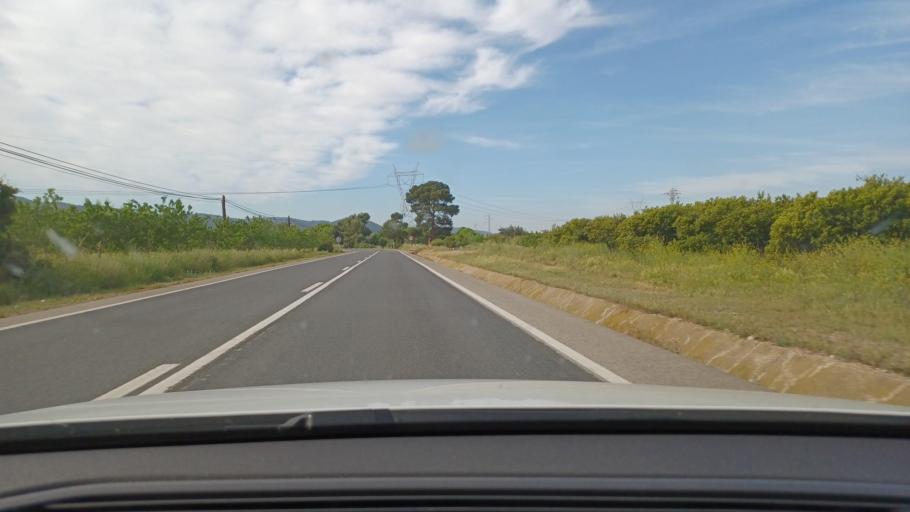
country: ES
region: Catalonia
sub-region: Provincia de Tarragona
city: Santa Barbara
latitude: 40.6950
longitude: 0.4756
